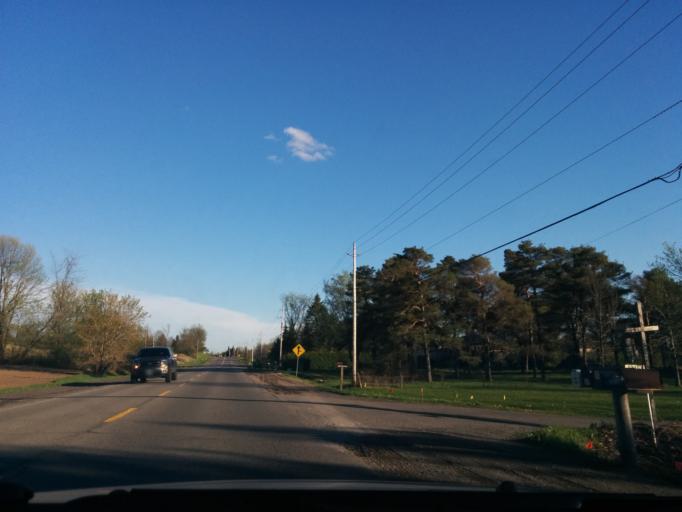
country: CA
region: Ontario
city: Bells Corners
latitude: 45.2257
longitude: -75.6679
